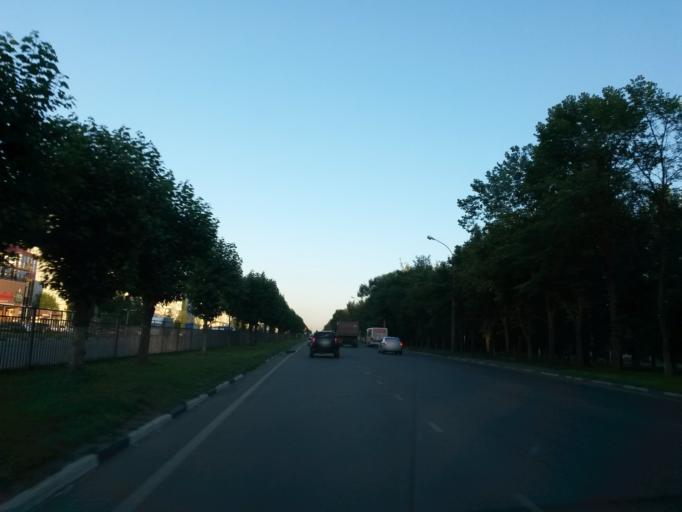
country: RU
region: Jaroslavl
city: Yaroslavl
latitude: 57.6939
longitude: 39.7706
